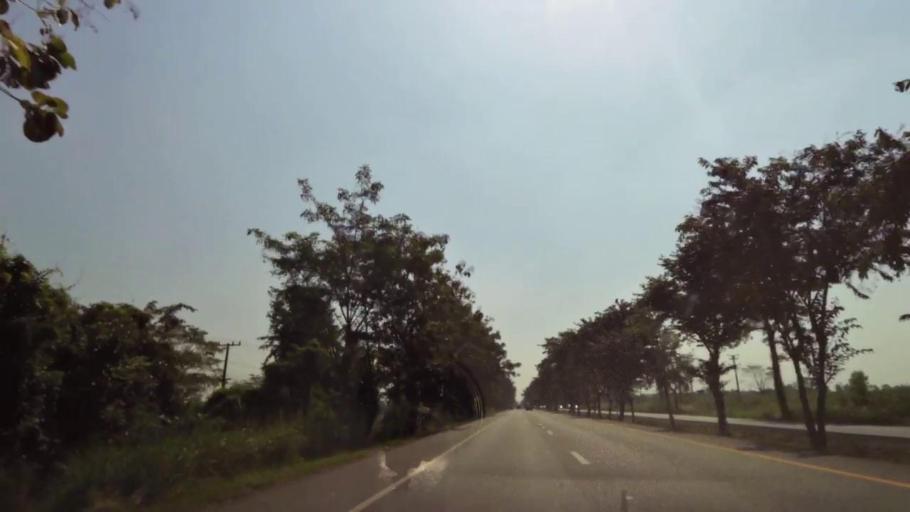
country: TH
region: Phichit
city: Bueng Na Rang
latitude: 16.0837
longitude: 100.1247
